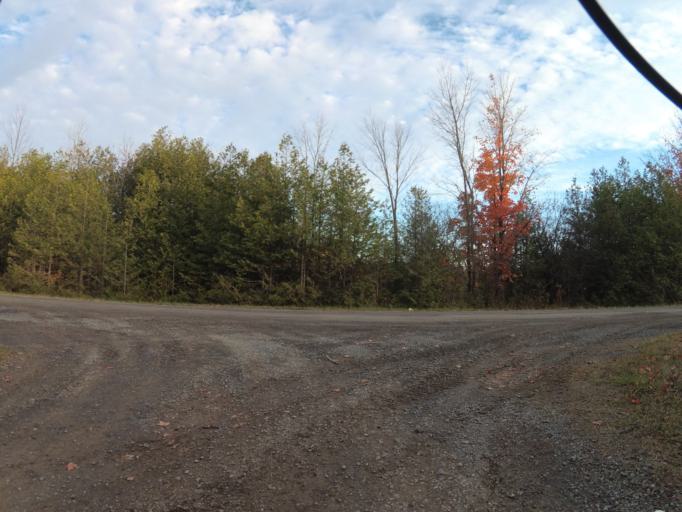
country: CA
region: Ontario
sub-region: Lanark County
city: Smiths Falls
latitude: 44.9936
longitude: -75.8122
